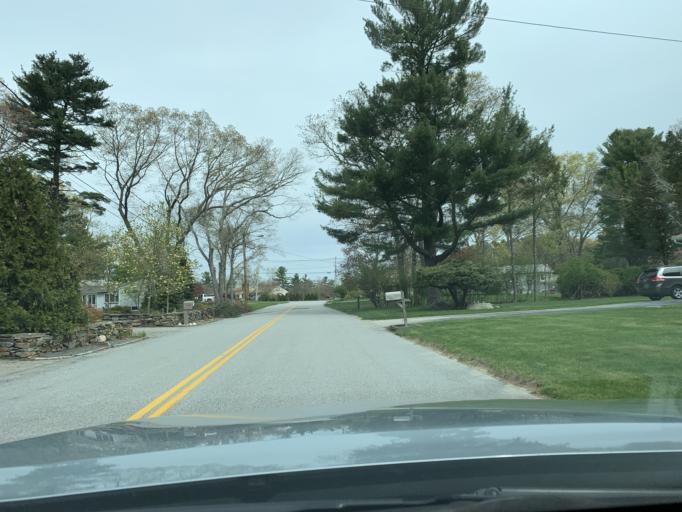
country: US
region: Rhode Island
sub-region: Washington County
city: North Kingstown
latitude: 41.6026
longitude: -71.4853
